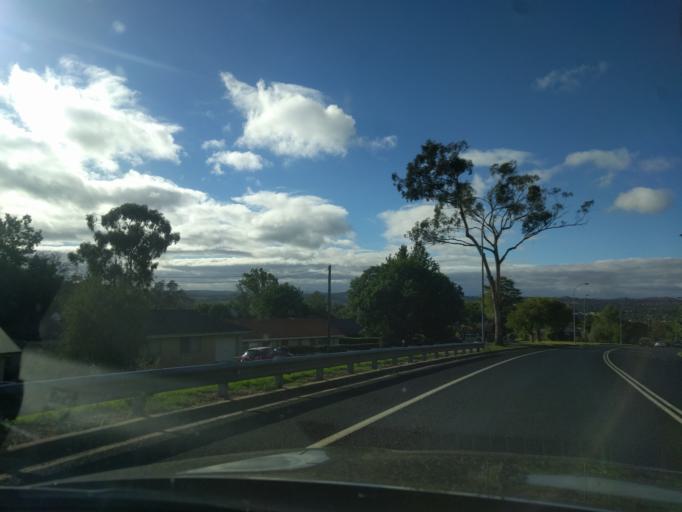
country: AU
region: New South Wales
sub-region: Armidale Dumaresq
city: Armidale
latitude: -30.4979
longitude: 151.6708
